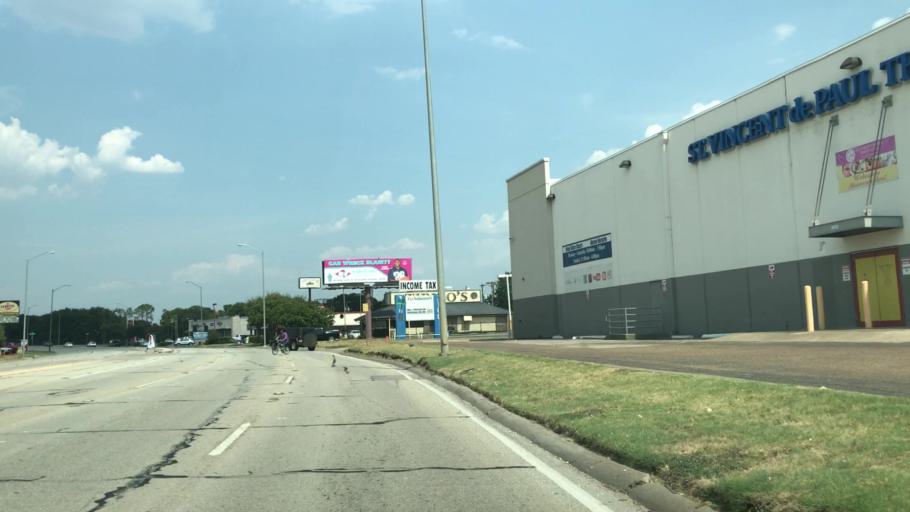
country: US
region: Texas
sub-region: Dallas County
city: University Park
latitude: 32.8550
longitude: -96.8690
